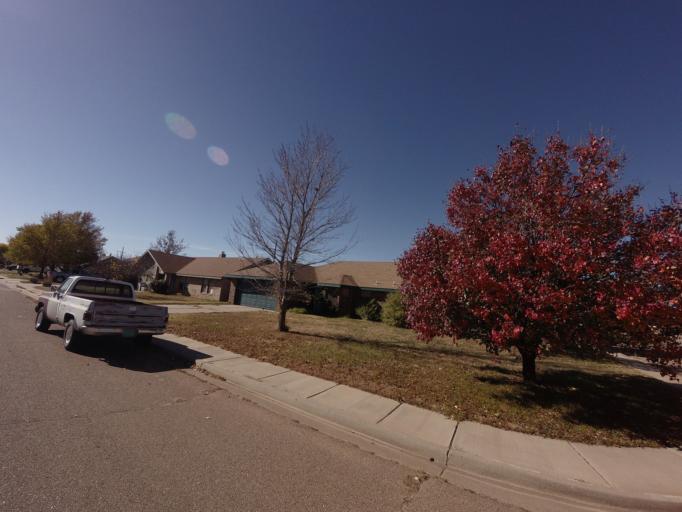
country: US
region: New Mexico
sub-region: Curry County
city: Clovis
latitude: 34.4143
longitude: -103.1694
